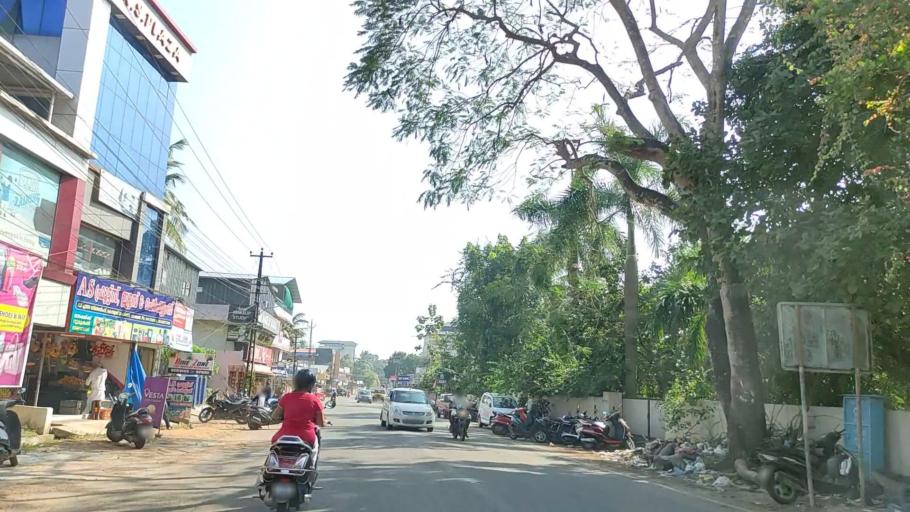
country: IN
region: Kerala
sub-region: Kollam
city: Punalur
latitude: 8.9267
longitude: 76.9191
